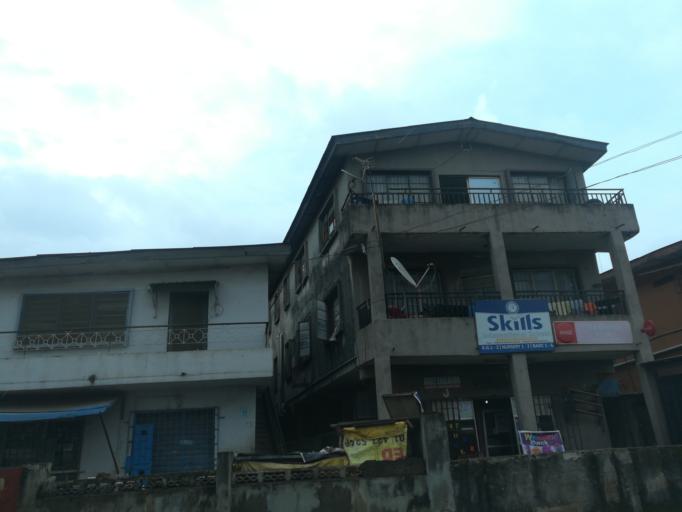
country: NG
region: Lagos
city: Oshodi
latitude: 6.5714
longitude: 3.3435
